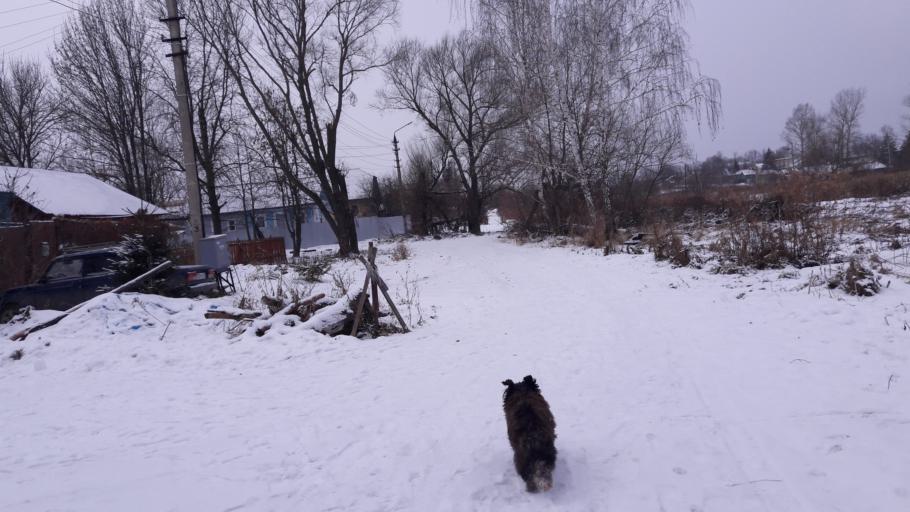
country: RU
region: Tula
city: Gorelki
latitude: 54.2360
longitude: 37.6372
